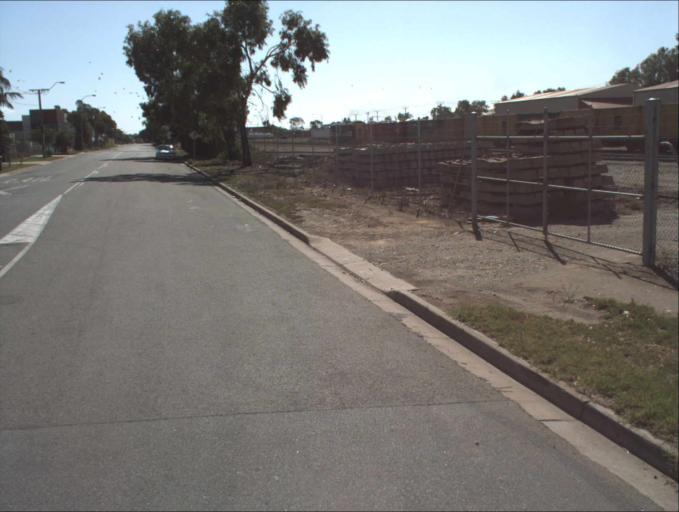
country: AU
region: South Australia
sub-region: Charles Sturt
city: Woodville North
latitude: -34.8401
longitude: 138.5505
